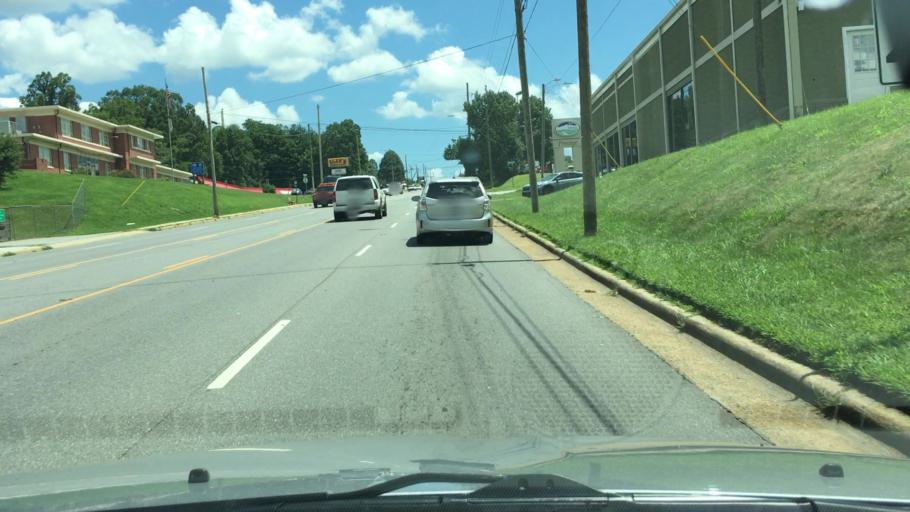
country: US
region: North Carolina
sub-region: Buncombe County
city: Asheville
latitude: 35.5867
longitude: -82.5116
